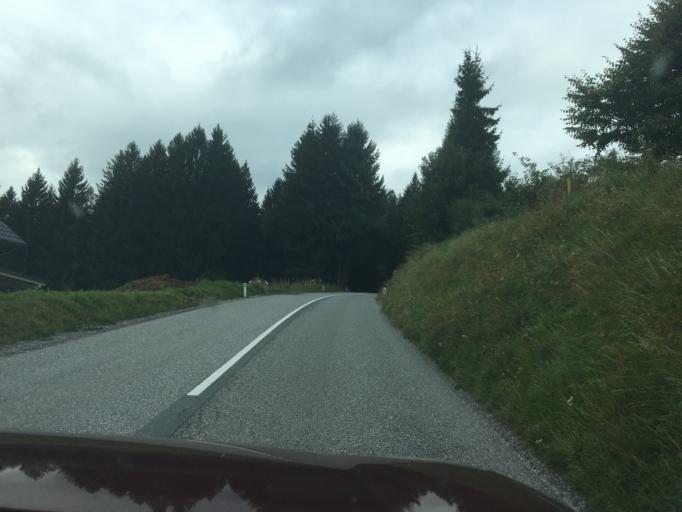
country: AT
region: Styria
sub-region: Politischer Bezirk Deutschlandsberg
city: Trahutten
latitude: 46.8236
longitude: 15.1508
